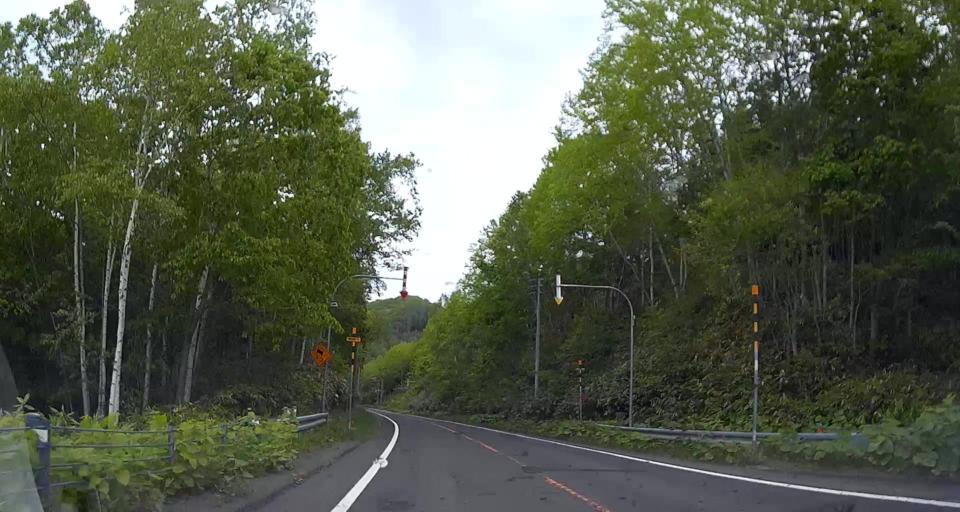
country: JP
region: Hokkaido
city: Date
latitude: 42.7223
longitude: 141.0721
